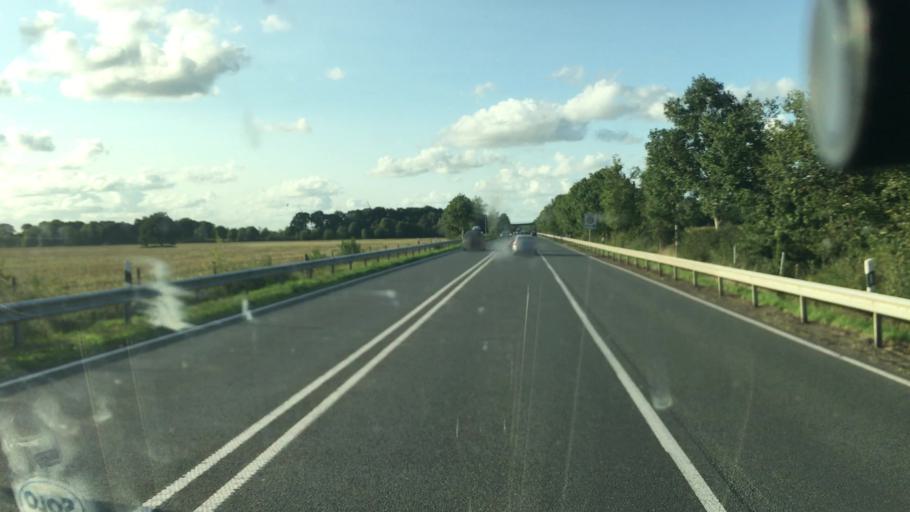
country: DE
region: Lower Saxony
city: Schortens
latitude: 53.5653
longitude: 7.9383
